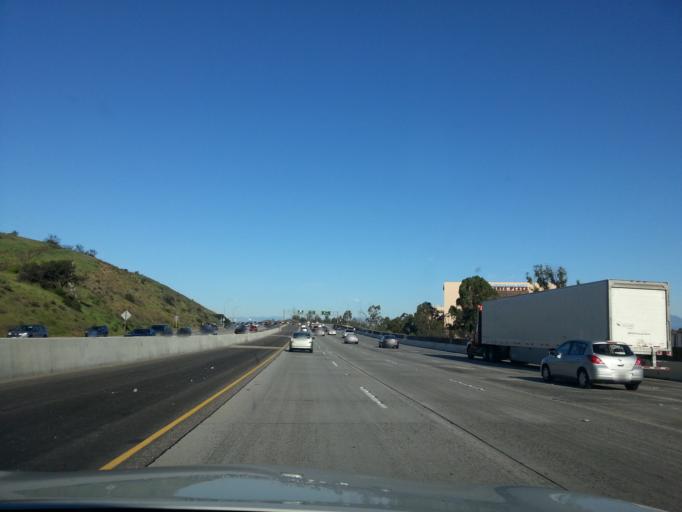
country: US
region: California
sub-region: Ventura County
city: Thousand Oaks
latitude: 34.1726
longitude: -118.8475
